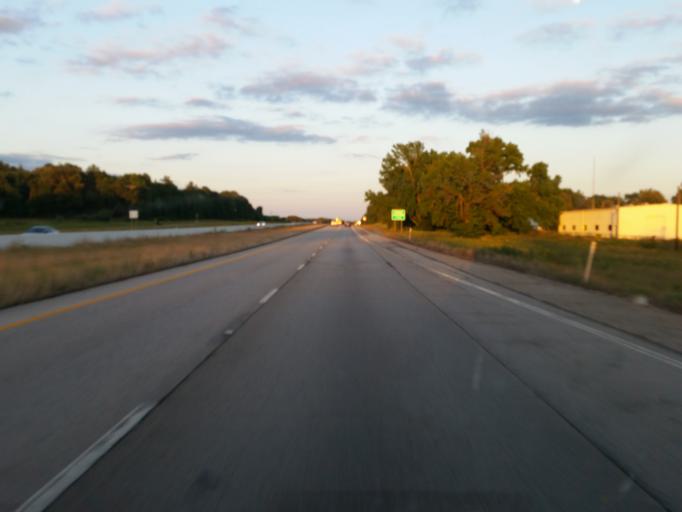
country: US
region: Texas
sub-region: Van Zandt County
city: Van
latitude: 32.4977
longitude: -95.5800
